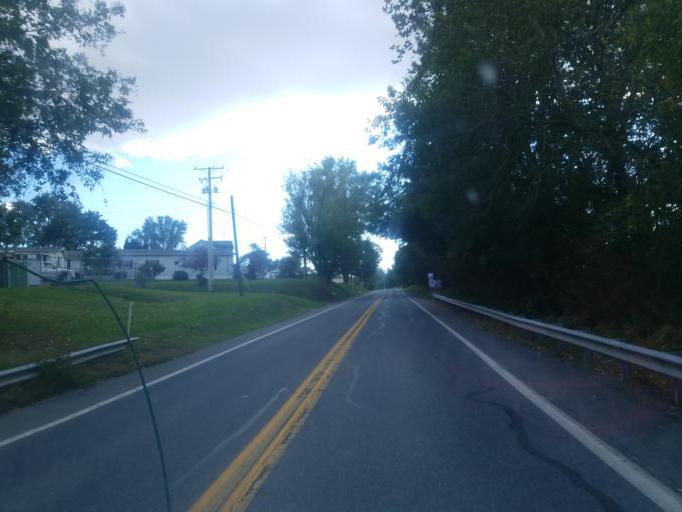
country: US
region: Pennsylvania
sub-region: Lancaster County
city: Bainbridge
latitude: 40.1320
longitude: -76.7142
